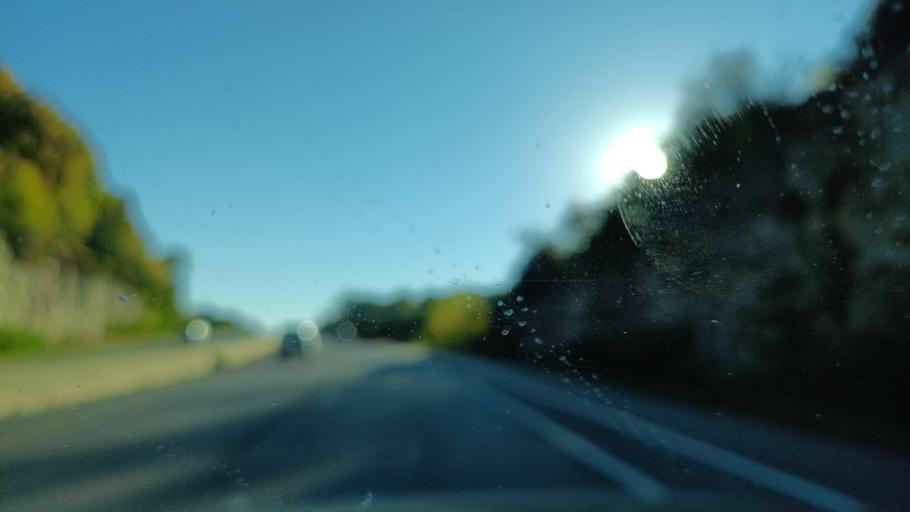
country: US
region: Missouri
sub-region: Boone County
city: Columbia
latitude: 38.9304
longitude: -92.3069
